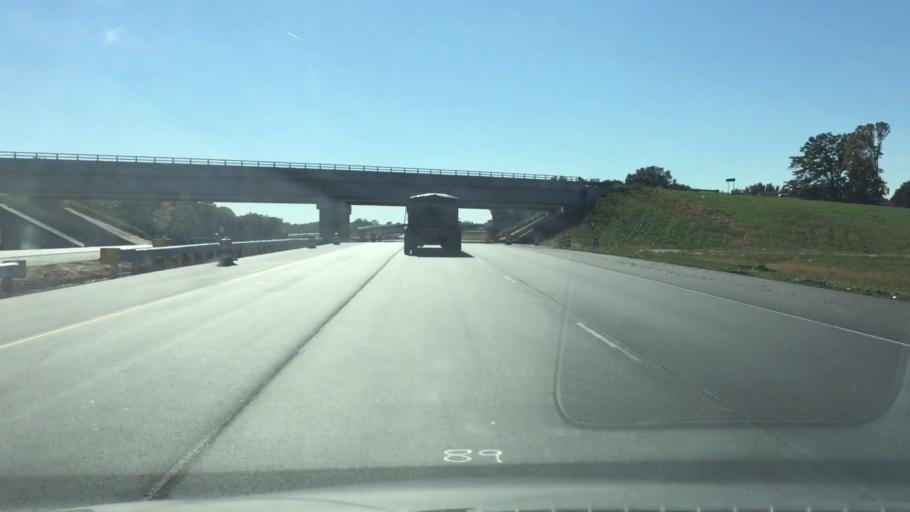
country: US
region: North Carolina
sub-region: Guilford County
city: McLeansville
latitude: 36.1523
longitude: -79.7289
